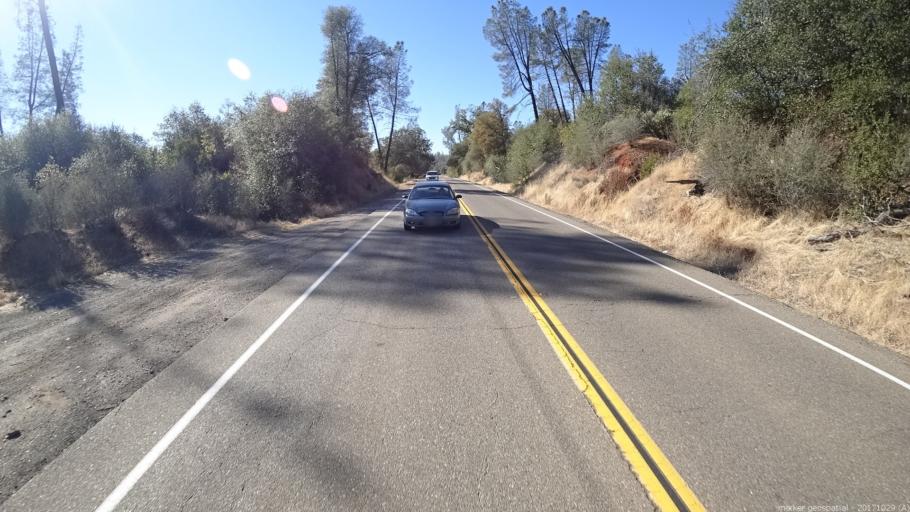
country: US
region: California
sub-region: Shasta County
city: Shasta
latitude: 40.4947
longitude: -122.4652
